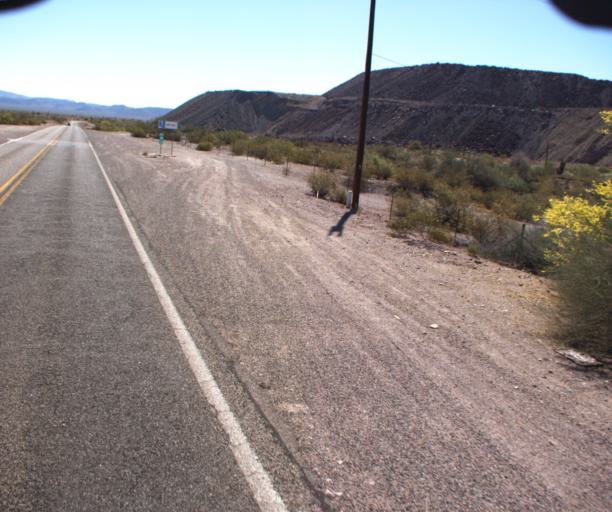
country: US
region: Arizona
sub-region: Pima County
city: Ajo
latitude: 32.3691
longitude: -112.8515
